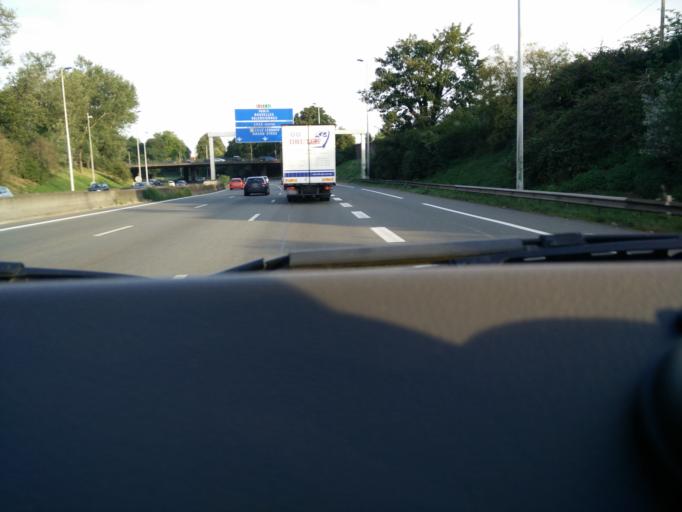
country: FR
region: Nord-Pas-de-Calais
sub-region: Departement du Nord
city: Loos
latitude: 50.6195
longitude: 3.0288
